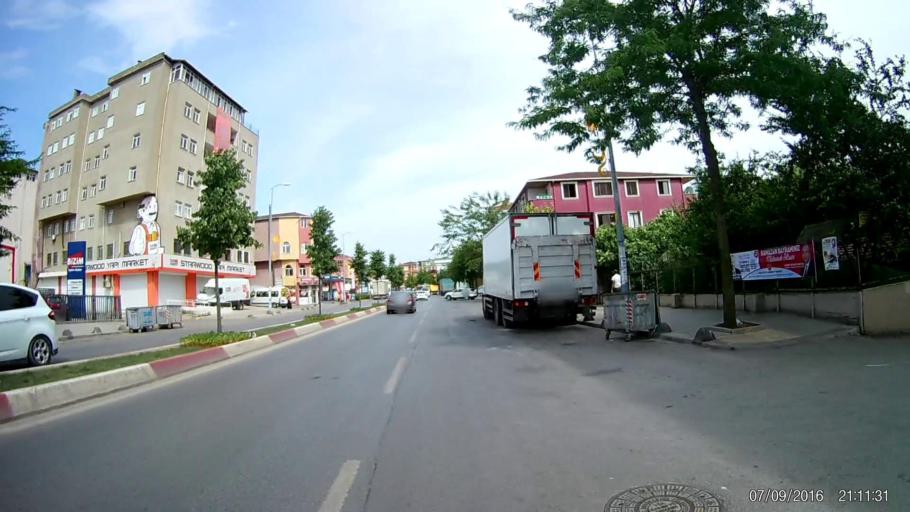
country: TR
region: Istanbul
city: Sultanbeyli
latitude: 40.9644
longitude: 29.2800
